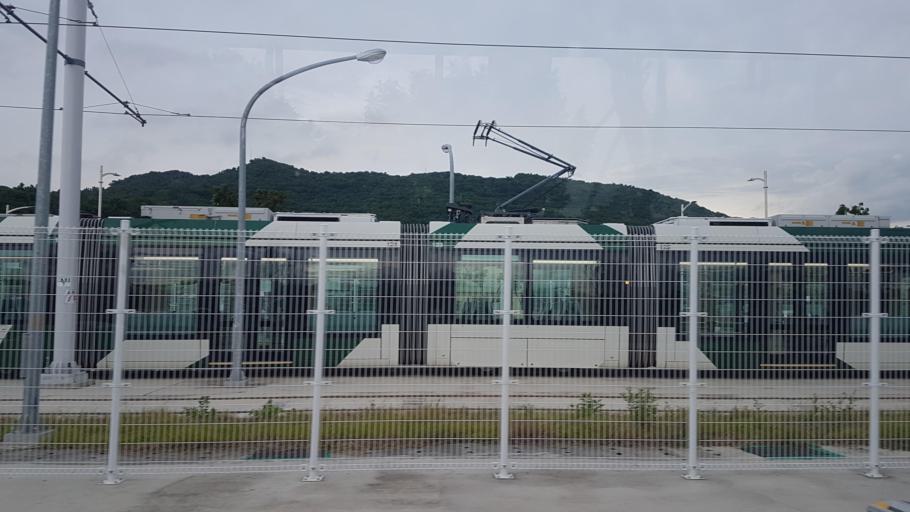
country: TW
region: Kaohsiung
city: Kaohsiung
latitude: 22.6439
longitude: 120.2811
